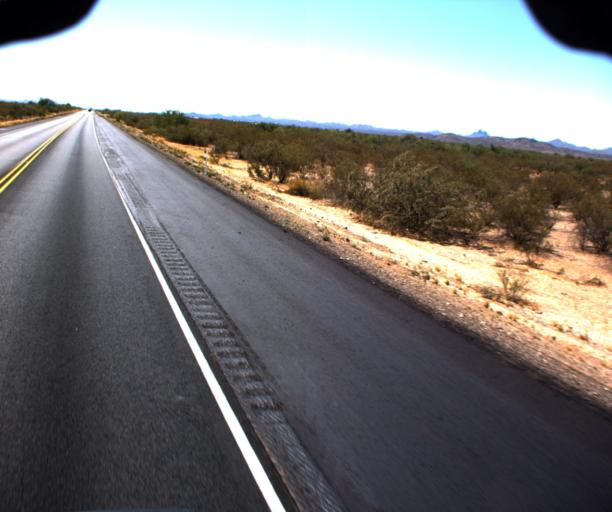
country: US
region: Arizona
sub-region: Yavapai County
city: Congress
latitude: 34.0542
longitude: -112.8512
